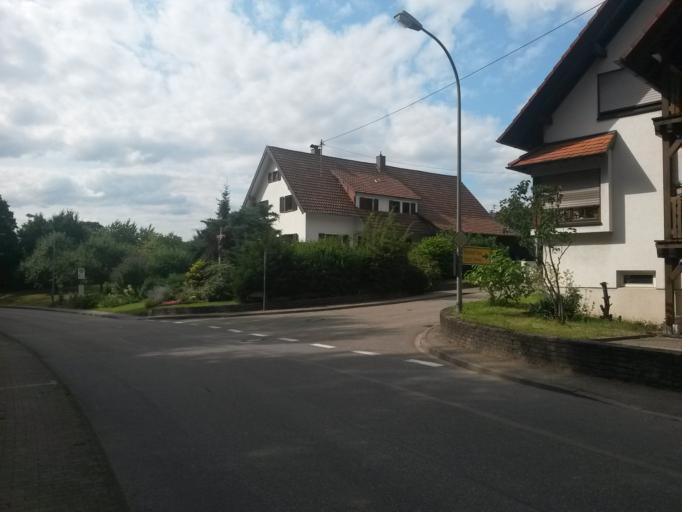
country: DE
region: Baden-Wuerttemberg
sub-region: Karlsruhe Region
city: Sinzheim
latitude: 48.7253
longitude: 8.1737
